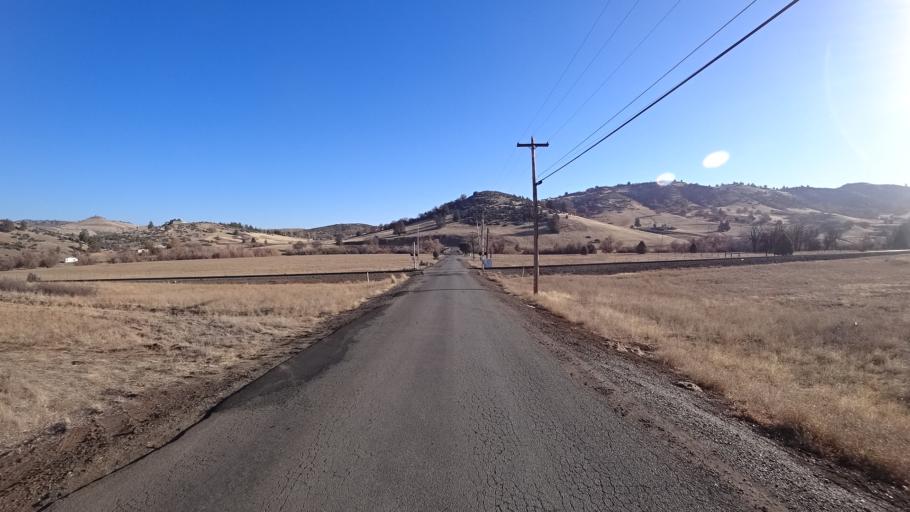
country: US
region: California
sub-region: Siskiyou County
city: Montague
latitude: 41.8889
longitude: -122.4845
